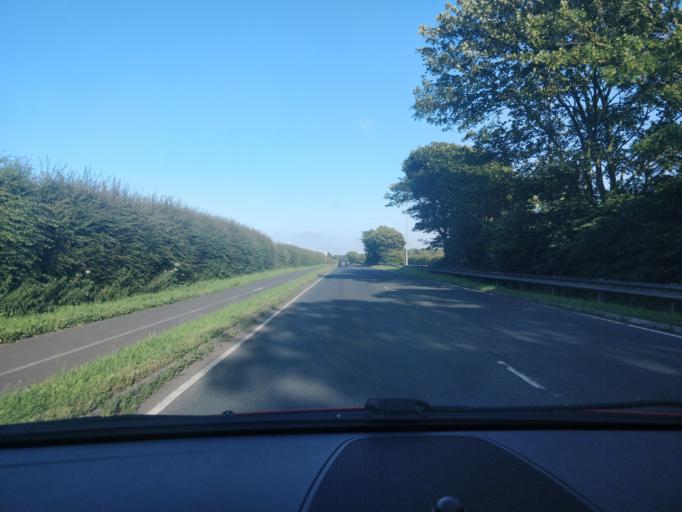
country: GB
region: England
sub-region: Lancashire
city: Banks
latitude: 53.6716
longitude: -2.9156
